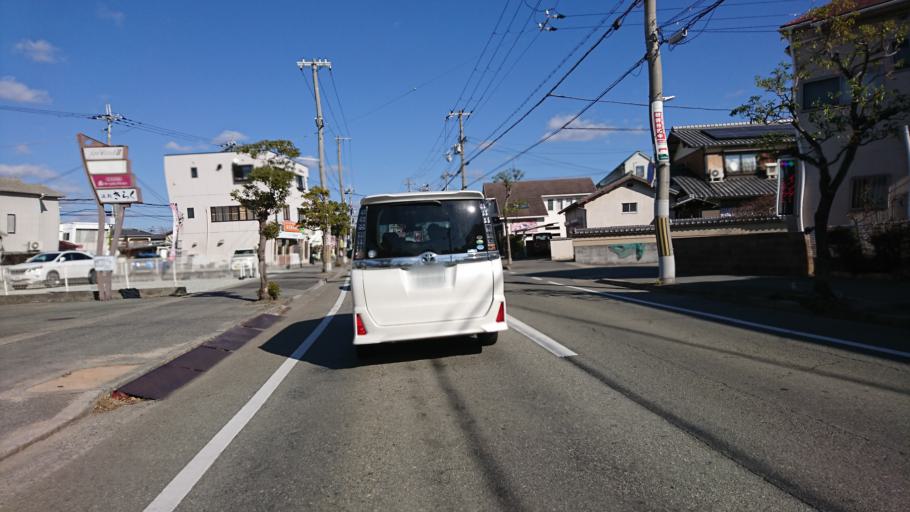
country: JP
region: Hyogo
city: Kakogawacho-honmachi
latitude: 34.7362
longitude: 134.8599
